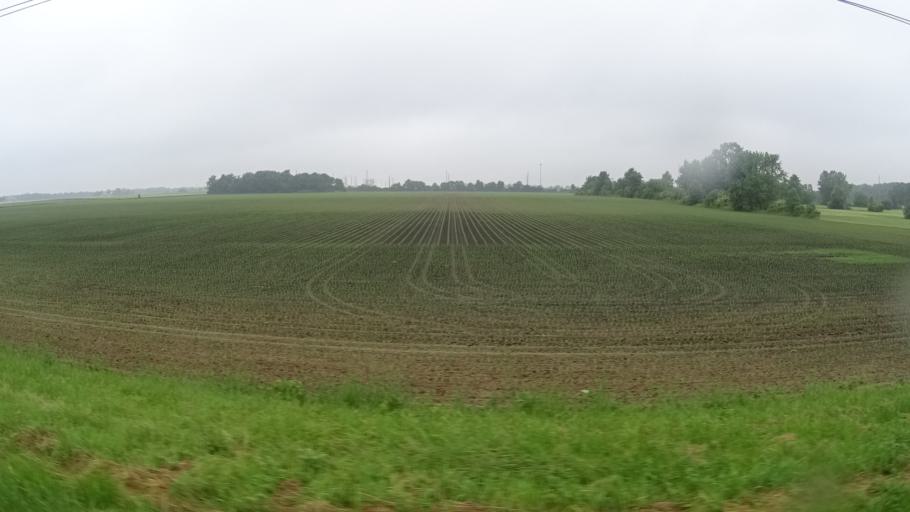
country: US
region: Ohio
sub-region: Huron County
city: Bellevue
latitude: 41.3263
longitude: -82.8332
